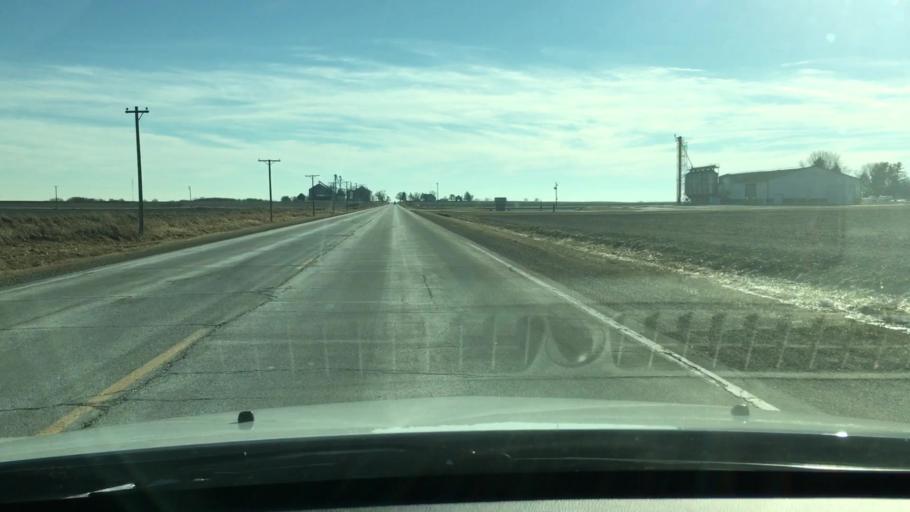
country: US
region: Illinois
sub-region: LaSalle County
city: Mendota
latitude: 41.6020
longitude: -89.1286
